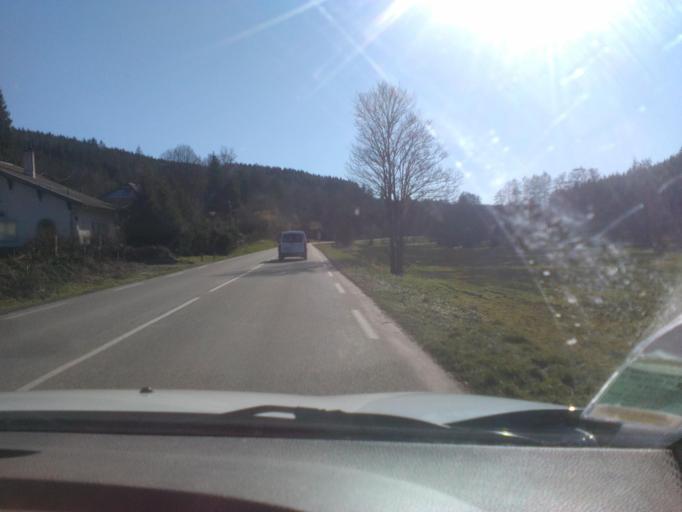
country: FR
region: Alsace
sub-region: Departement du Bas-Rhin
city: Rothau
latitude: 48.4014
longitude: 7.1549
